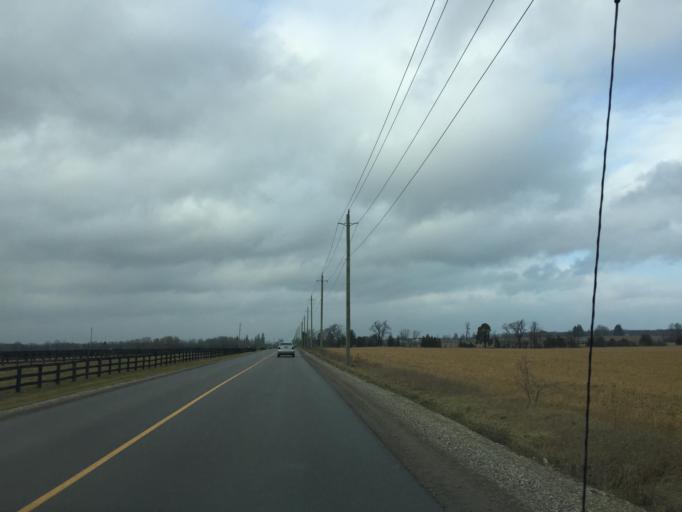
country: CA
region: Ontario
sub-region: Wellington County
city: Guelph
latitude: 43.4679
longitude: -80.3287
